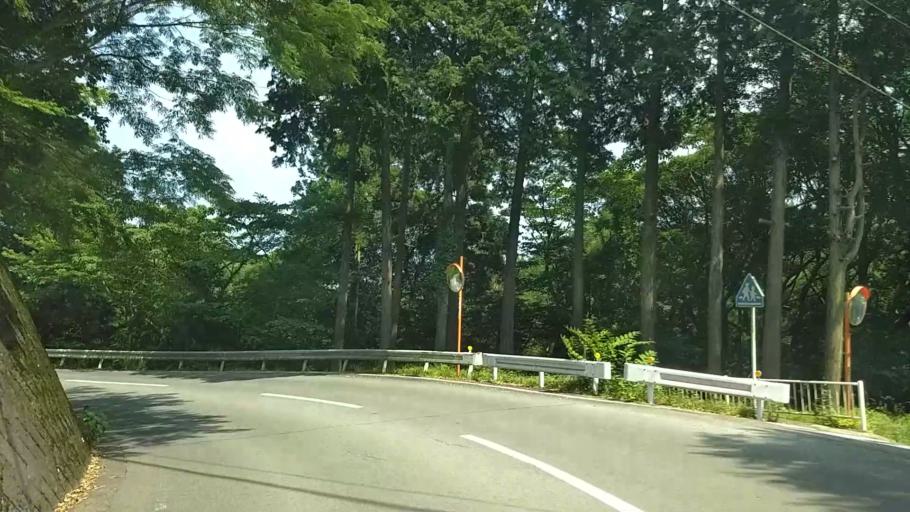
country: JP
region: Shizuoka
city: Ito
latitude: 34.9345
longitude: 139.1118
